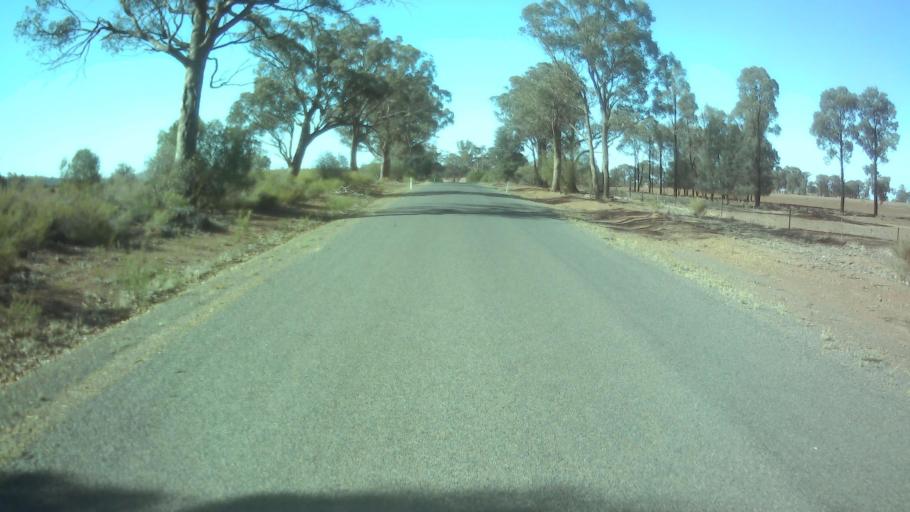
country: AU
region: New South Wales
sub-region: Forbes
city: Forbes
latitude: -33.6981
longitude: 147.8072
